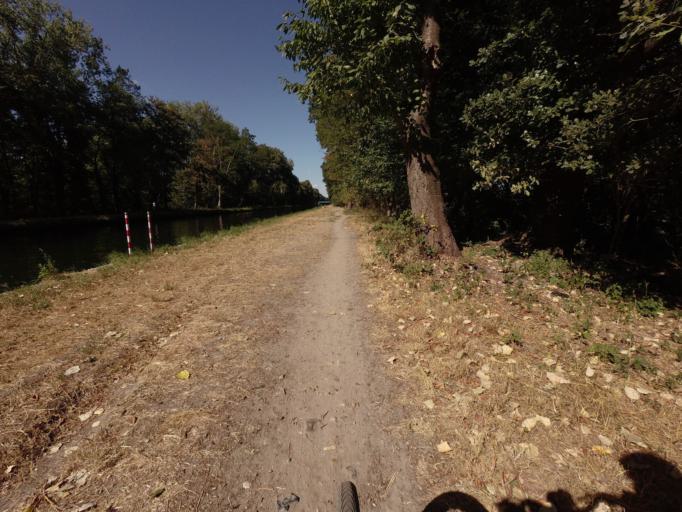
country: BE
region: Flanders
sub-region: Provincie Antwerpen
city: Turnhout
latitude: 51.3387
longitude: 4.9504
